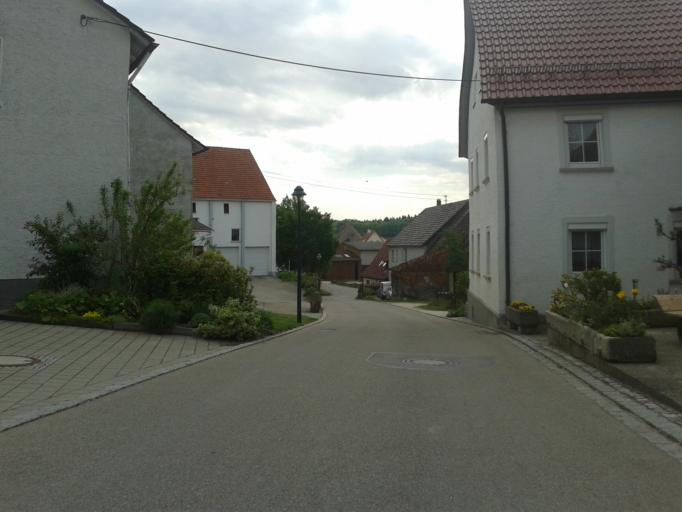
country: DE
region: Baden-Wuerttemberg
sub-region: Tuebingen Region
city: Blaubeuren
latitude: 48.3802
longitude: 9.8048
